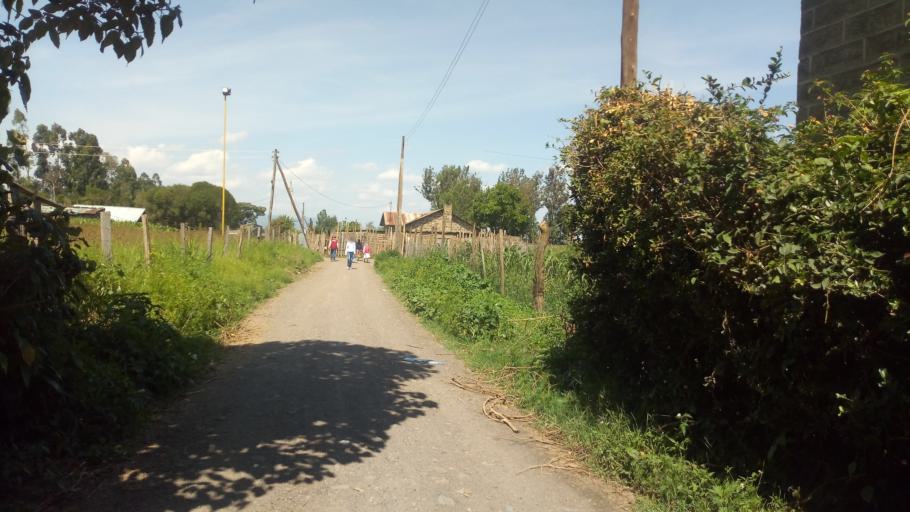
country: KE
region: Nakuru
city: Nakuru
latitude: -0.2763
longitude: 36.1201
